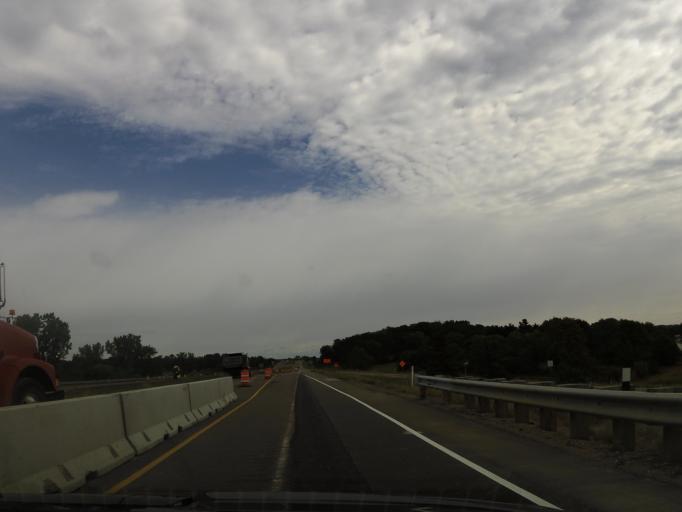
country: US
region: Wisconsin
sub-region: Monroe County
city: Tomah
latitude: 43.9730
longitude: -90.4715
